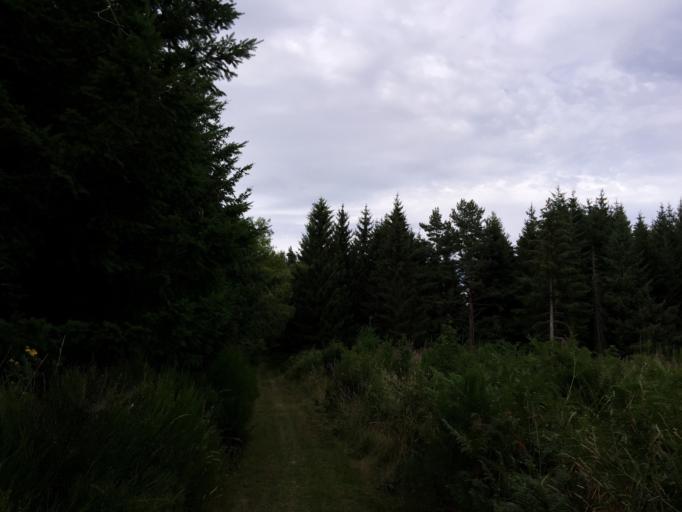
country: FR
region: Rhone-Alpes
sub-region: Departement de la Loire
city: Saint-Bonnet-le-Chateau
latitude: 45.3887
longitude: 4.0373
